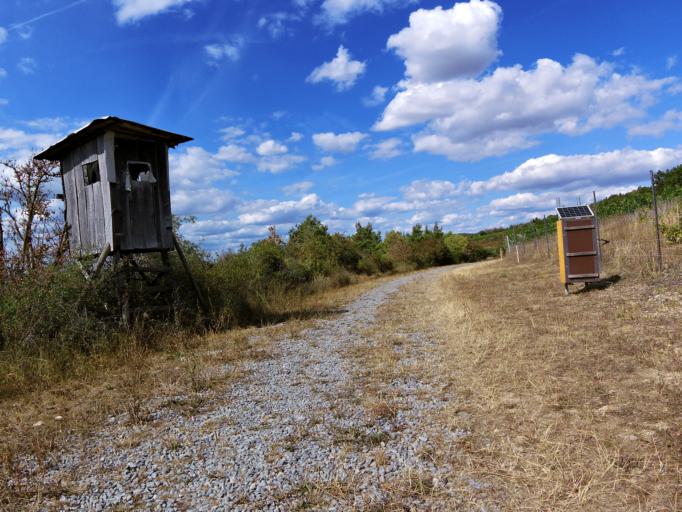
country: DE
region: Bavaria
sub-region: Regierungsbezirk Unterfranken
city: Erlabrunn
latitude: 49.8573
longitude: 9.8603
